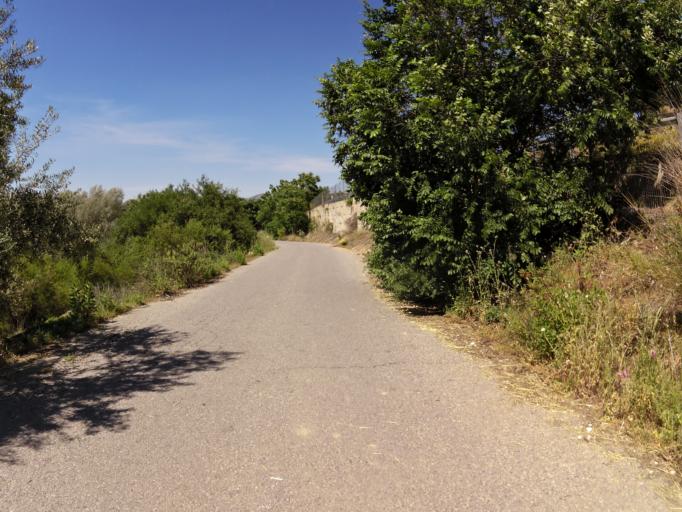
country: ES
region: Andalusia
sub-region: Provincia de Granada
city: Salar
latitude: 37.1777
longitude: -4.0813
